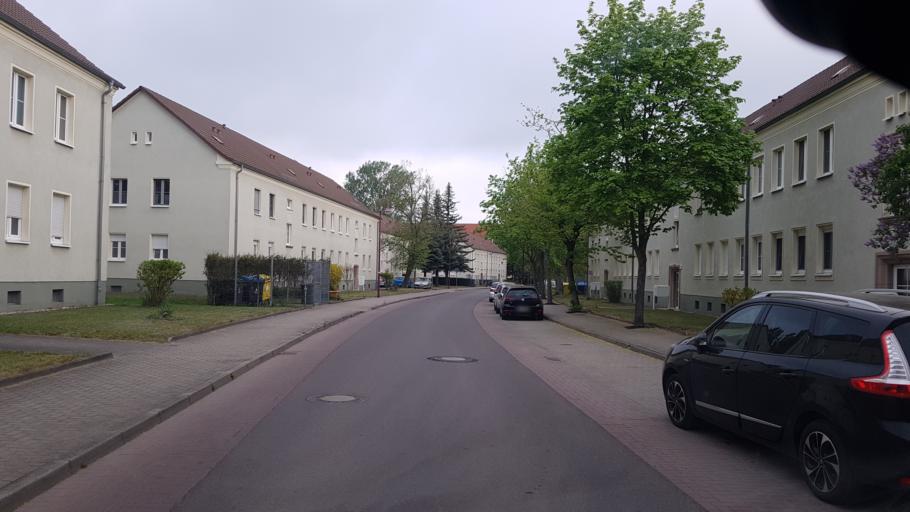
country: DE
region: Brandenburg
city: Grossraschen
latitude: 51.5868
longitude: 13.9973
